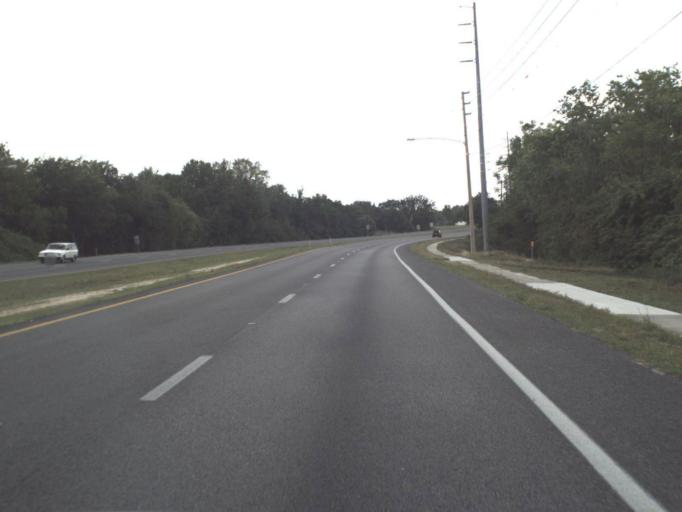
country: US
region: Florida
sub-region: Lake County
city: Eustis
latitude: 28.8661
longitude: -81.6874
